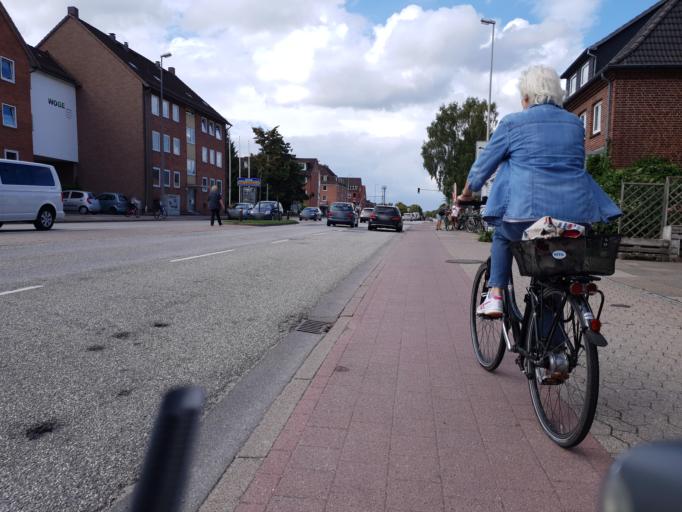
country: DE
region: Schleswig-Holstein
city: Kronshagen
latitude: 54.3433
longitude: 10.0996
